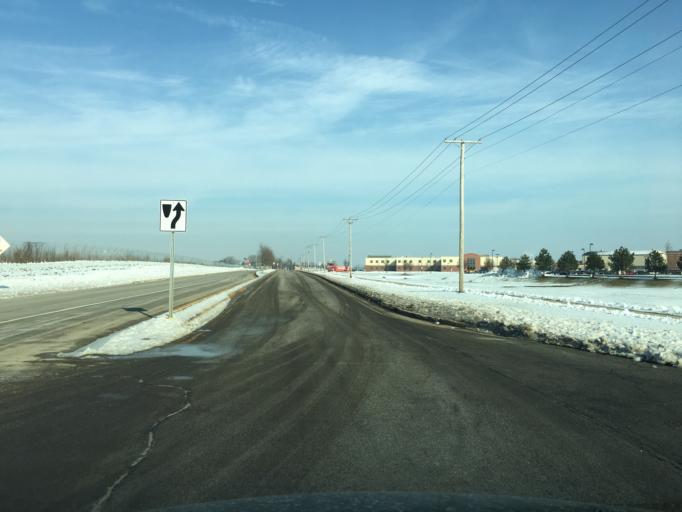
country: US
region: Illinois
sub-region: Will County
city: Plainfield
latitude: 41.6619
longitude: -88.1773
